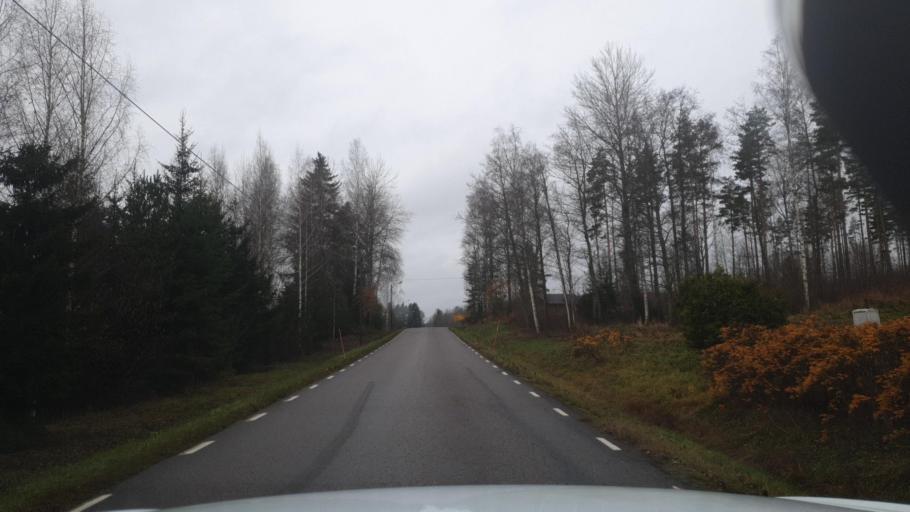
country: SE
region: Vaermland
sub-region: Arvika Kommun
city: Arvika
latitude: 59.5700
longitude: 12.5126
